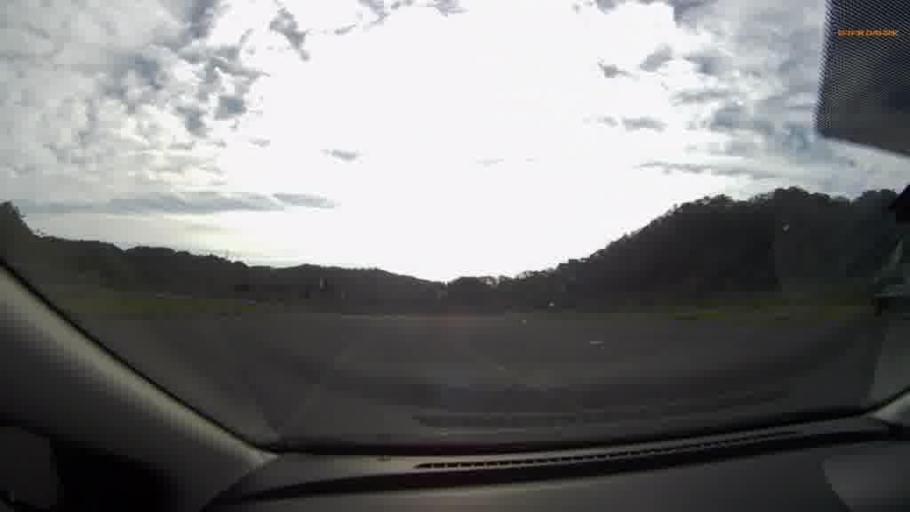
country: JP
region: Hokkaido
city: Kushiro
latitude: 43.0771
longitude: 143.9631
